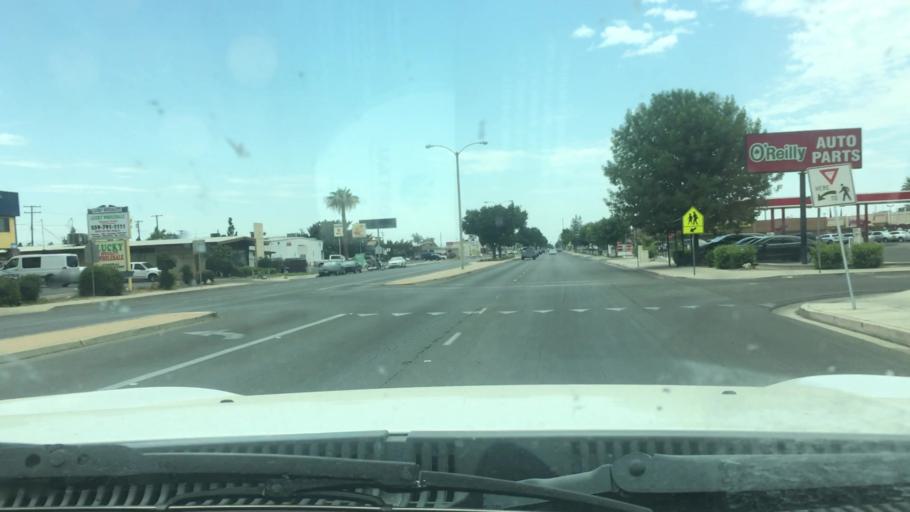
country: US
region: California
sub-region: Tulare County
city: Porterville
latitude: 36.0659
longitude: -119.0444
